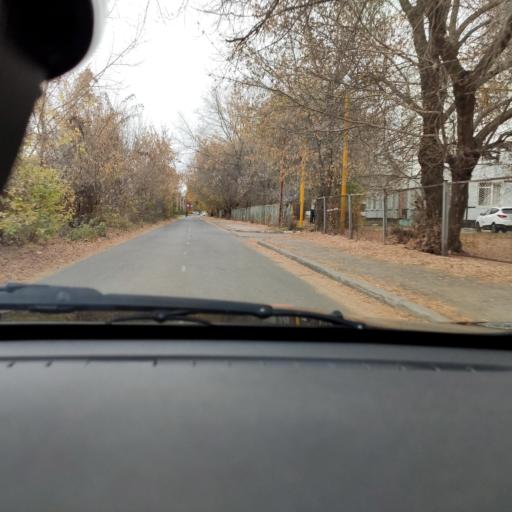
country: RU
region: Samara
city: Tol'yatti
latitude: 53.5278
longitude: 49.3913
